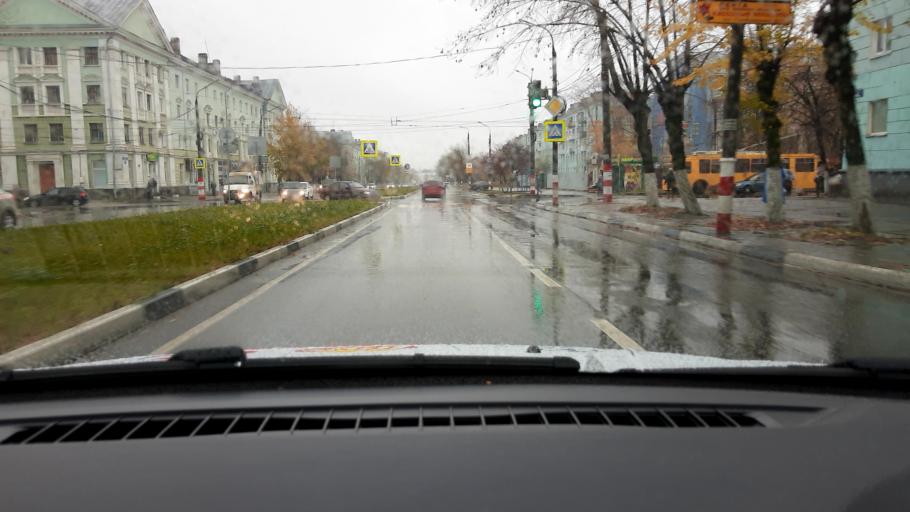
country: RU
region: Nizjnij Novgorod
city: Dzerzhinsk
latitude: 56.2403
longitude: 43.4500
